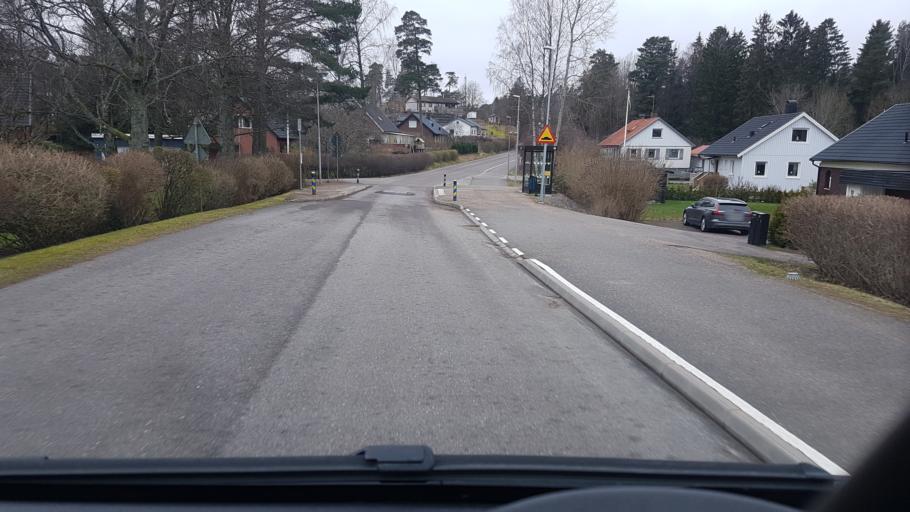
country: SE
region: Vaestra Goetaland
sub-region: Lerums Kommun
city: Stenkullen
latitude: 57.7981
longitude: 12.3625
